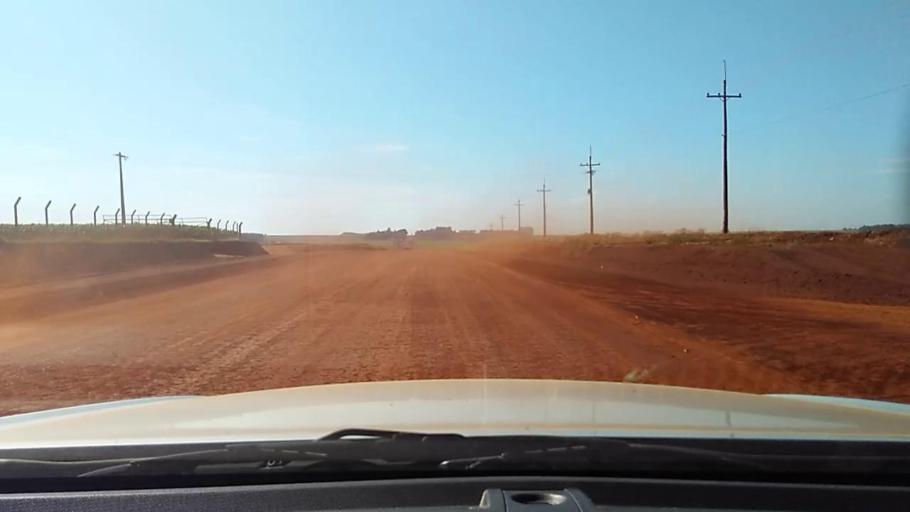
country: PY
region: Alto Parana
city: Naranjal
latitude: -25.9214
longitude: -55.4135
